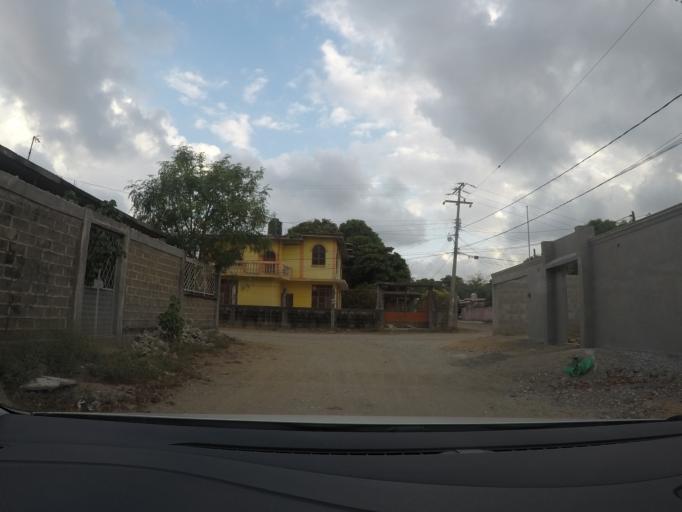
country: MX
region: Oaxaca
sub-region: Salina Cruz
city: Salina Cruz
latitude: 16.2095
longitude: -95.1964
